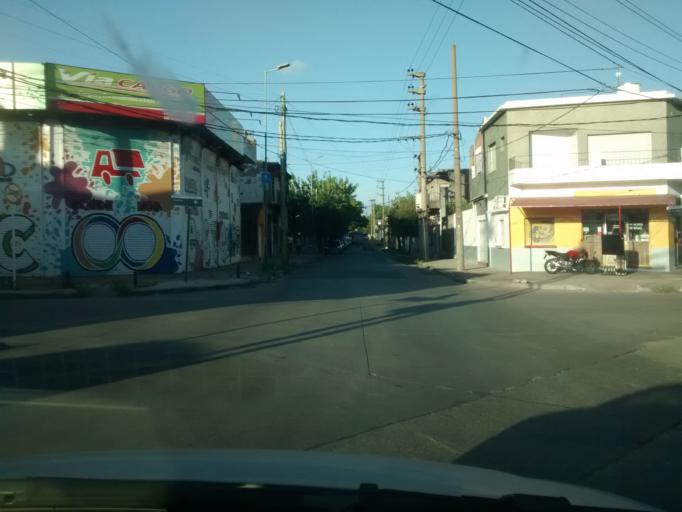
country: AR
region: Buenos Aires
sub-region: Partido de Moron
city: Moron
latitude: -34.6603
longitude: -58.6123
